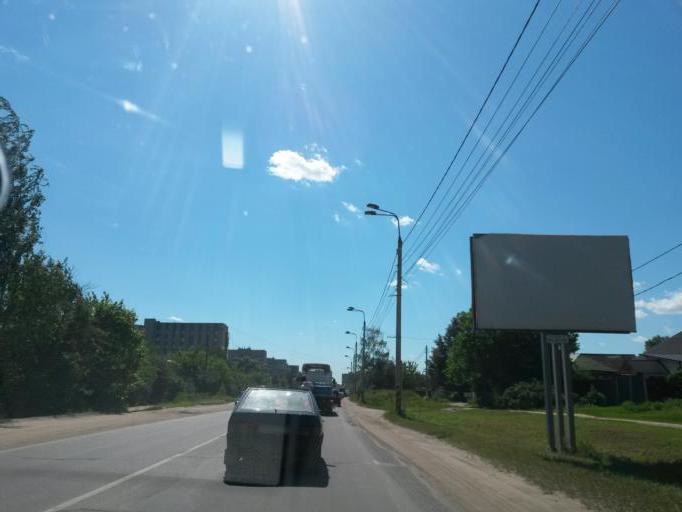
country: RU
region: Moskovskaya
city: Serpukhov
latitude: 54.9054
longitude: 37.3724
